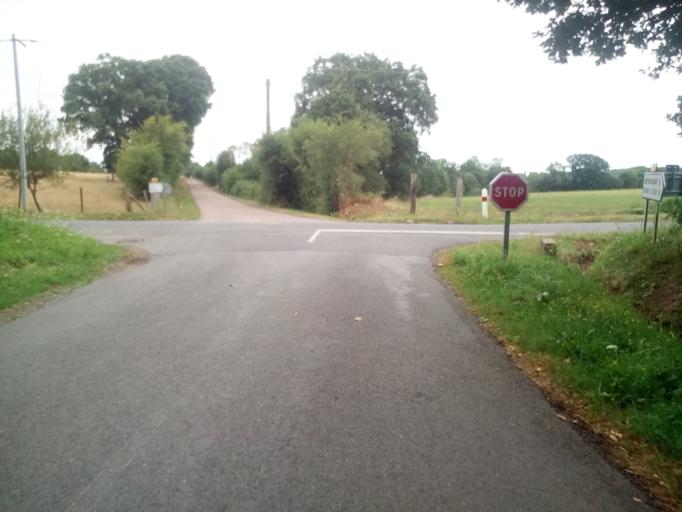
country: FR
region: Lower Normandy
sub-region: Departement du Calvados
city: Clinchamps-sur-Orne
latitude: 49.0311
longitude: -0.3939
